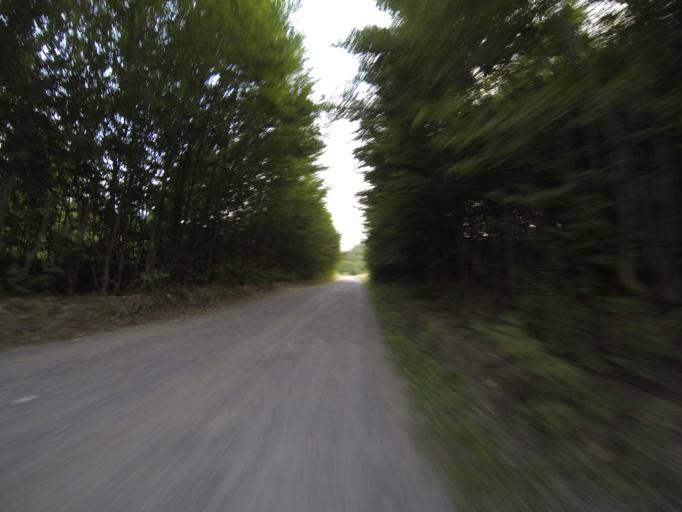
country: RO
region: Brasov
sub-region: Comuna Sinca Noua
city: Sinca Noua
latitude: 45.7338
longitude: 25.2891
